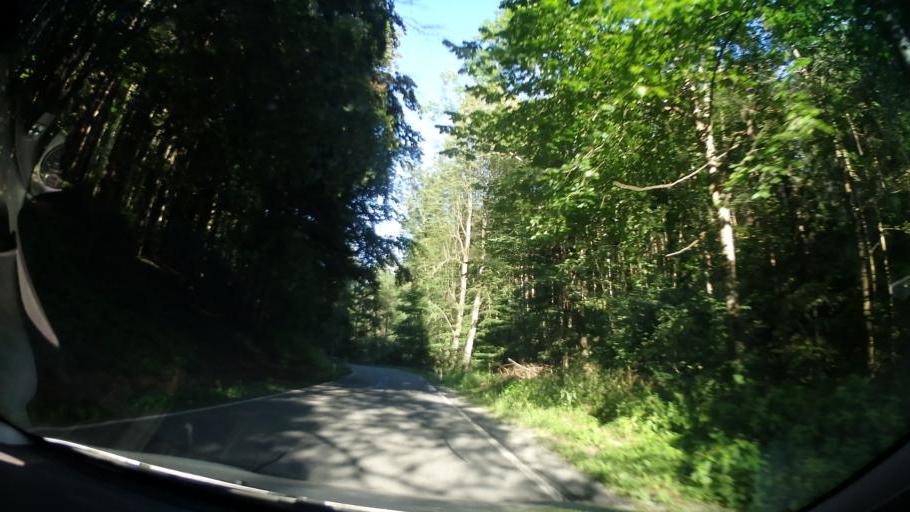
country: CZ
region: Olomoucky
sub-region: Okres Jesenik
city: Jesenik
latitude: 50.2049
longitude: 17.2398
